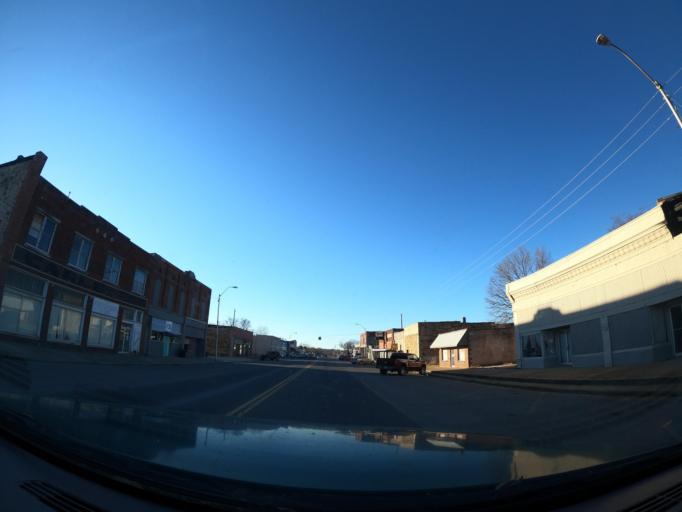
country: US
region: Oklahoma
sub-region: Pittsburg County
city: Hartshorne
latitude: 34.8454
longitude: -95.5572
